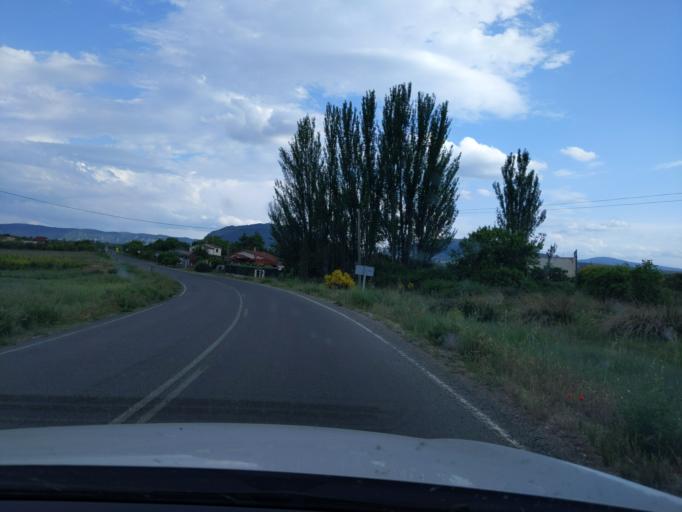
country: ES
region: La Rioja
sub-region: Provincia de La Rioja
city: Alberite
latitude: 42.3985
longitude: -2.4273
